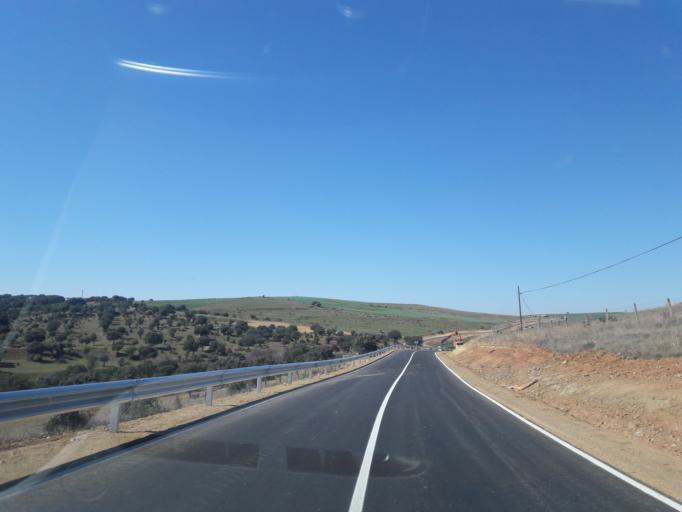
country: ES
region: Castille and Leon
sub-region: Provincia de Salamanca
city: Valdemierque
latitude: 40.8231
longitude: -5.5607
